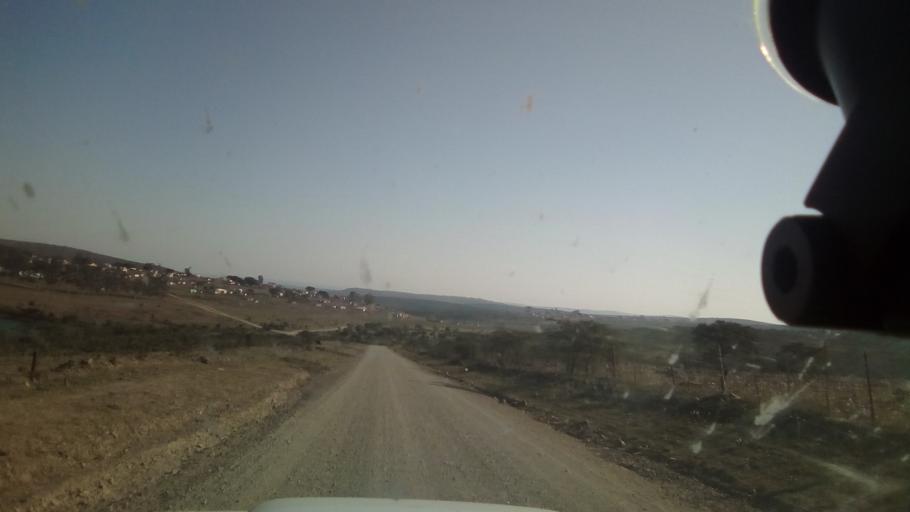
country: ZA
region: Eastern Cape
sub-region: Buffalo City Metropolitan Municipality
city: Bhisho
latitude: -32.9877
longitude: 27.2454
